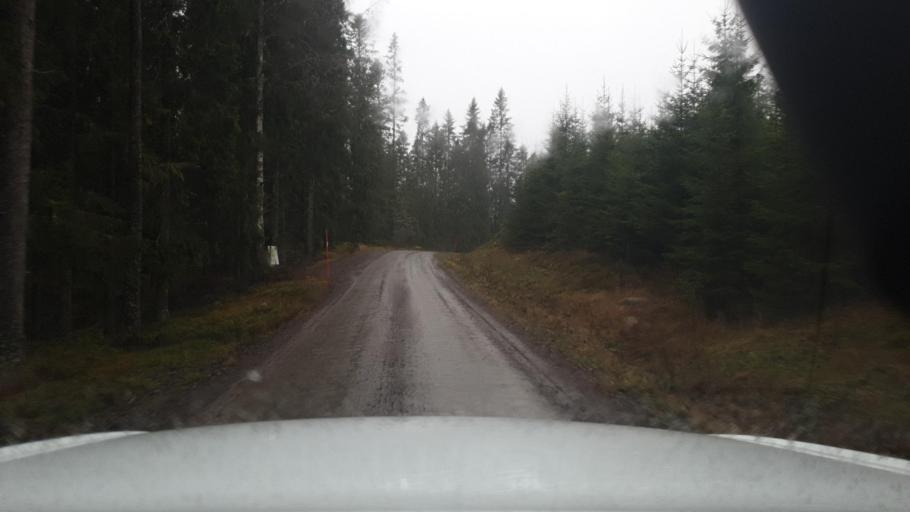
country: SE
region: Vaermland
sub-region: Sunne Kommun
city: Sunne
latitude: 59.8542
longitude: 12.8484
